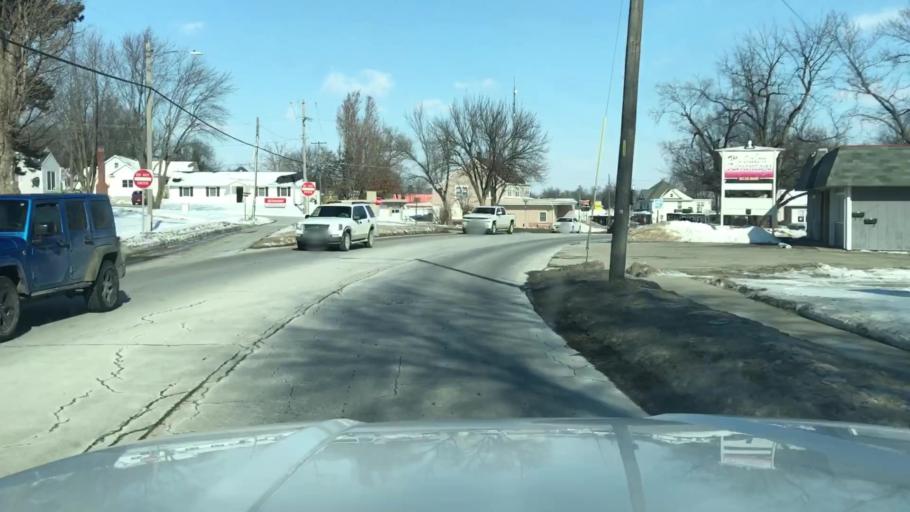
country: US
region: Missouri
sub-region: Nodaway County
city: Maryville
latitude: 40.3375
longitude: -94.8737
